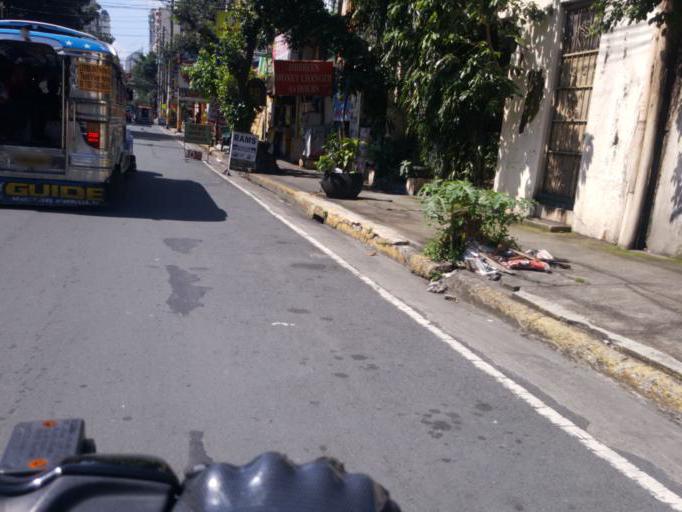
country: PH
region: Metro Manila
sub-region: City of Manila
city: Port Area
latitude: 14.5677
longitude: 120.9856
